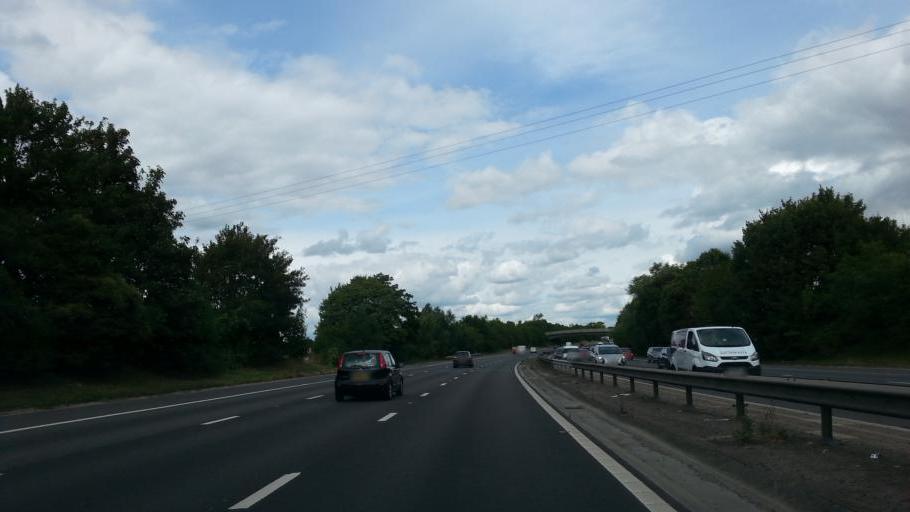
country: GB
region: England
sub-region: Essex
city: Little Hallingbury
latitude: 51.8065
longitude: 0.1765
